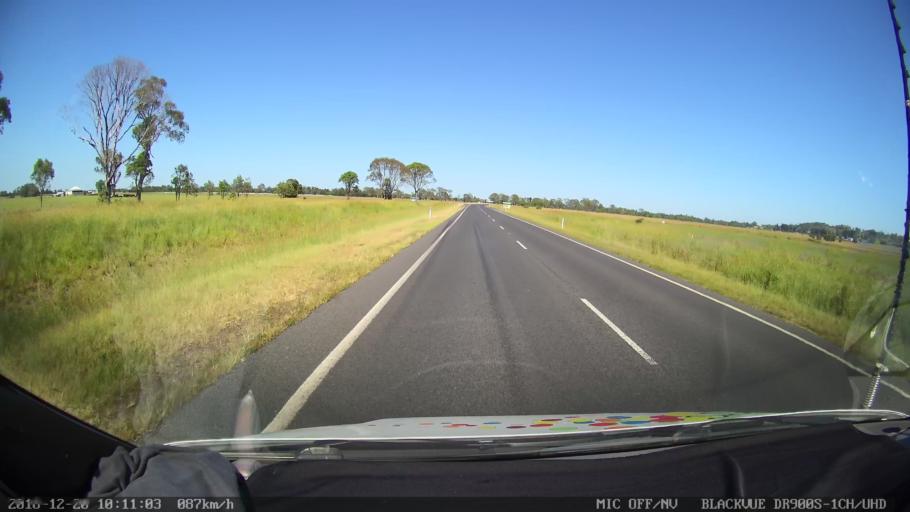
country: AU
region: New South Wales
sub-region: Richmond Valley
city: Casino
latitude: -28.8734
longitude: 153.1645
